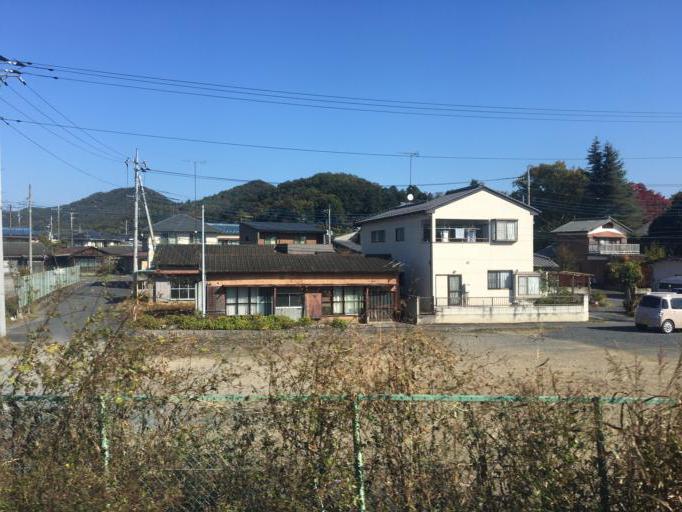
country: JP
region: Tochigi
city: Ashikaga
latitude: 36.3365
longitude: 139.4311
